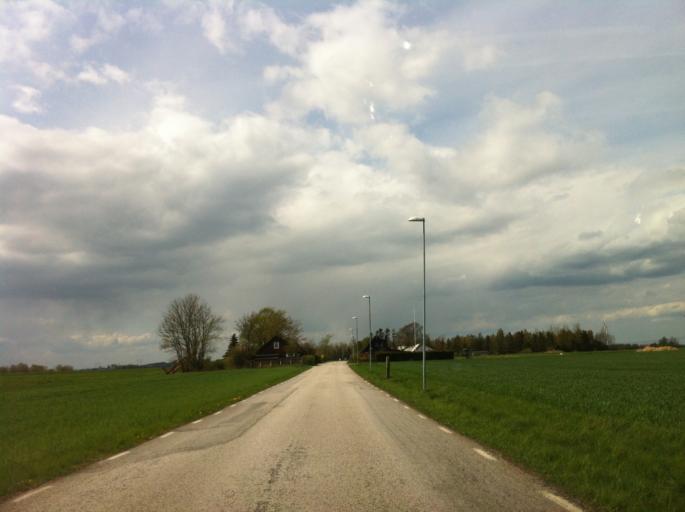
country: SE
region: Skane
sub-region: Kavlinge Kommun
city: Kaevlinge
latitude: 55.8085
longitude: 13.1494
